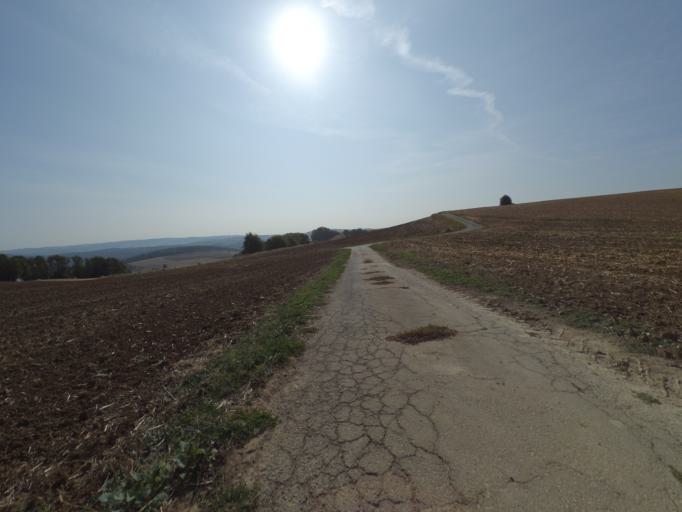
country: DE
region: Rheinland-Pfalz
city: Merzkirchen
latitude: 49.5701
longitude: 6.4844
